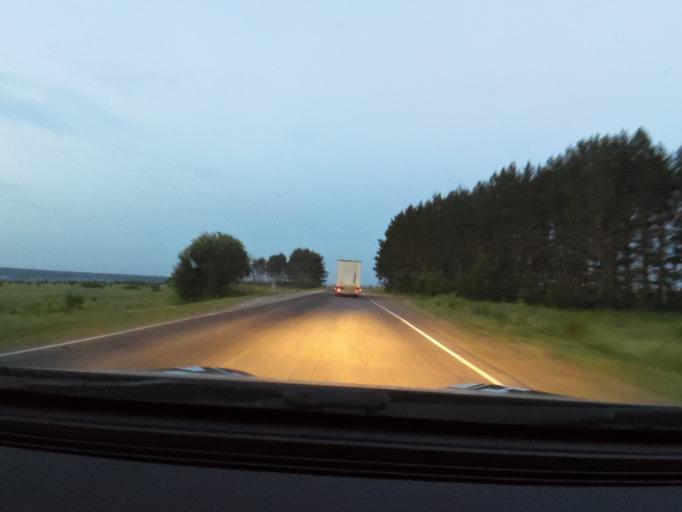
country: RU
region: Bashkortostan
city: Duvan
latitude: 56.0749
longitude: 58.1542
